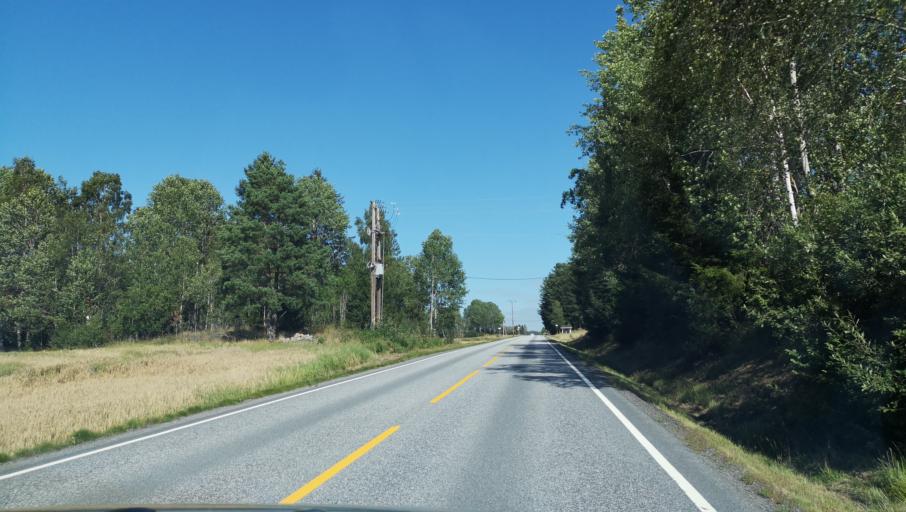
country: NO
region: Akershus
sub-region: Vestby
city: Vestby
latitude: 59.5447
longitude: 10.7893
